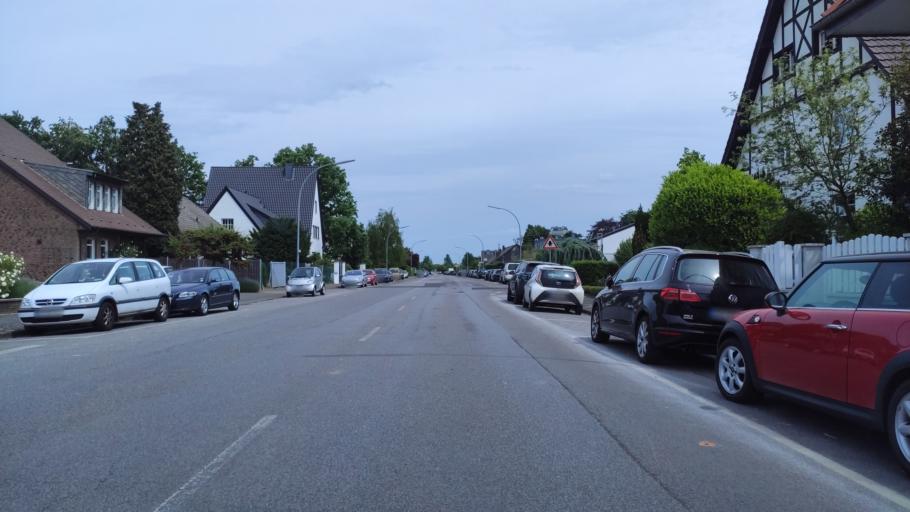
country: DE
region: North Rhine-Westphalia
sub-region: Regierungsbezirk Dusseldorf
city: Monchengladbach
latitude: 51.2145
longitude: 6.4160
